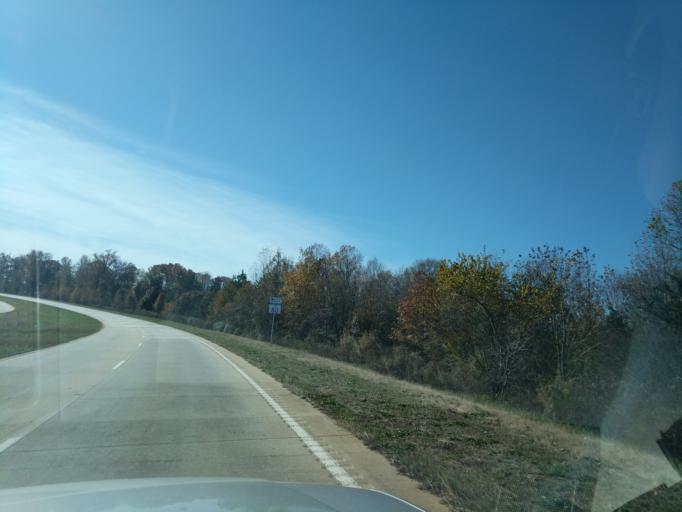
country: US
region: South Carolina
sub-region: Greenville County
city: Greer
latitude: 34.9093
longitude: -82.2179
